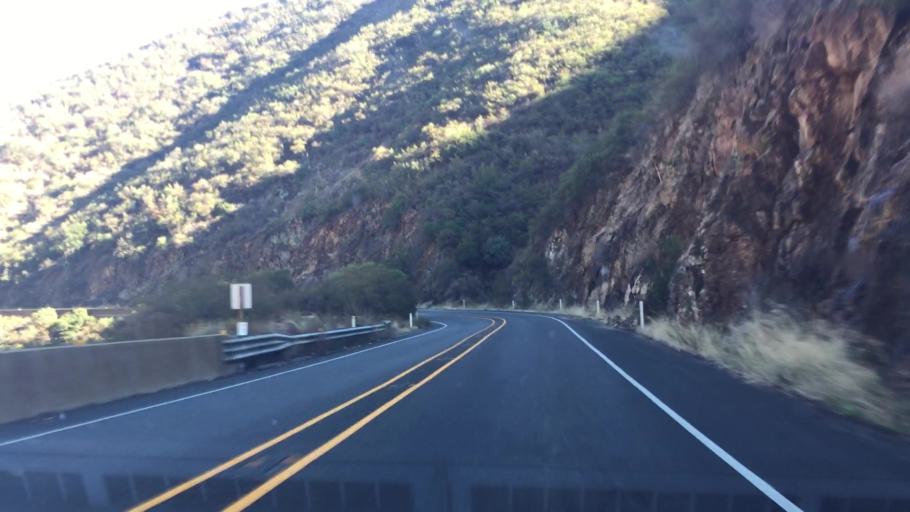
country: US
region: California
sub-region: Orange County
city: Coto De Caza
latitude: 33.5919
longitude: -117.4713
